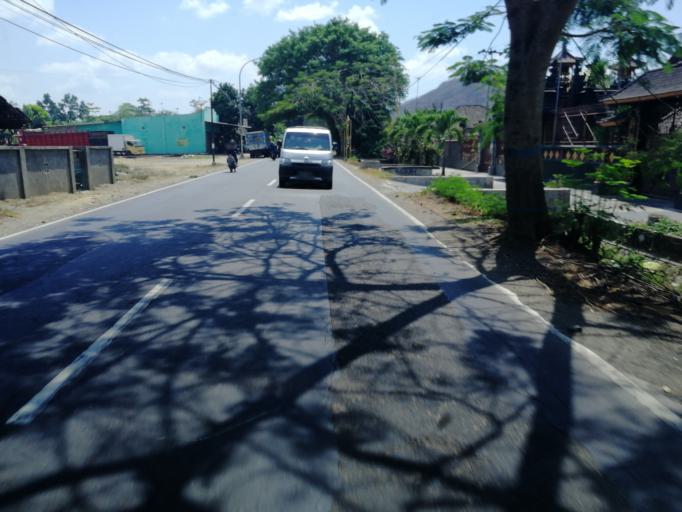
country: ID
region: West Nusa Tenggara
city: Jelateng Timur
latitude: -8.7011
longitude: 116.0994
